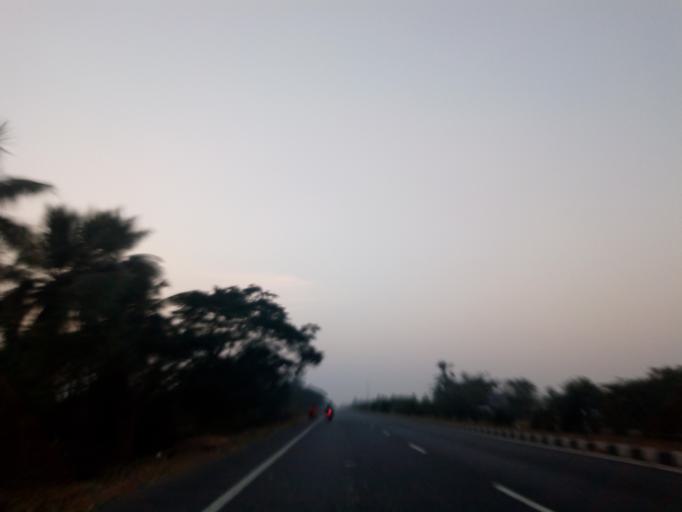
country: IN
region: Andhra Pradesh
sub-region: West Godavari
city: Tadepallegudem
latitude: 16.8241
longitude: 81.4456
